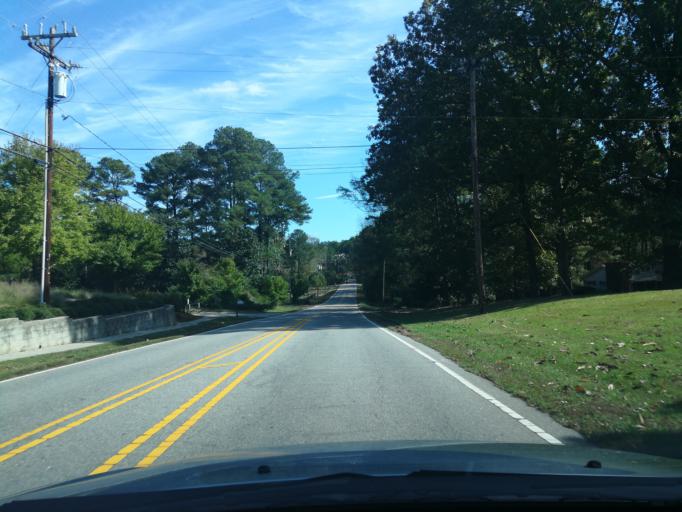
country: US
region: North Carolina
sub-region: Durham County
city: Durham
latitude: 35.9755
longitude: -78.9689
